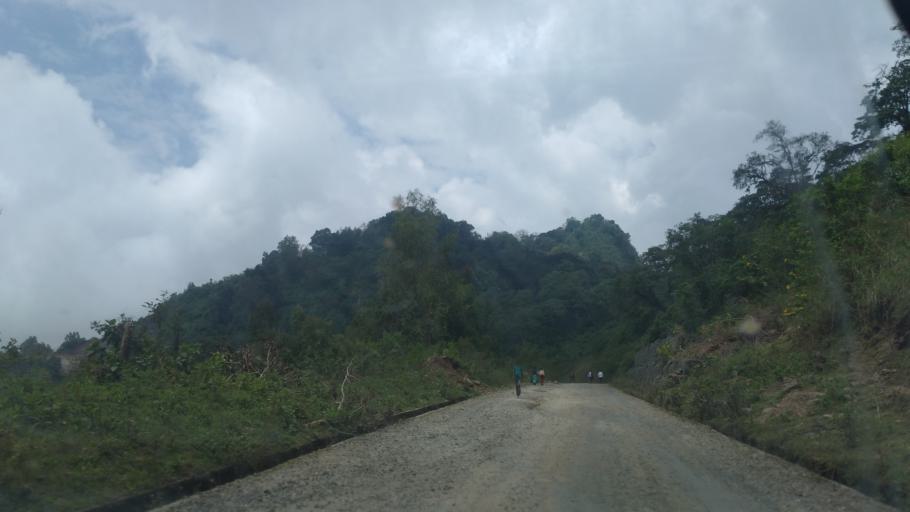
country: ET
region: Southern Nations, Nationalities, and People's Region
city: Bonga
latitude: 7.1134
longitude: 36.7264
